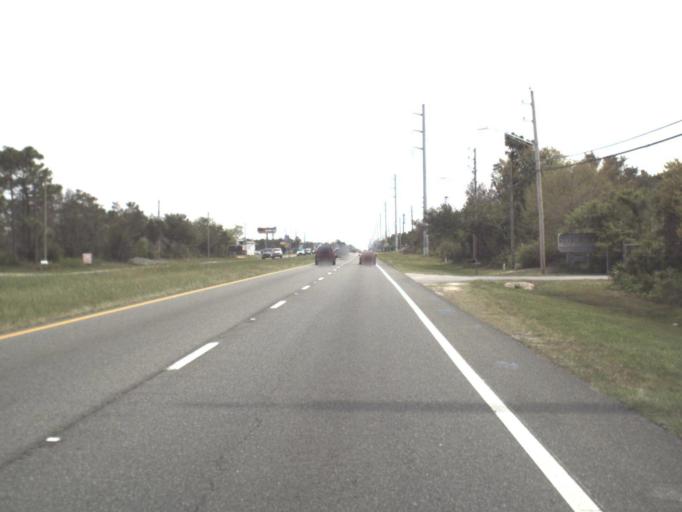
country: US
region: Florida
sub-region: Santa Rosa County
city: Tiger Point
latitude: 30.3919
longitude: -87.0522
